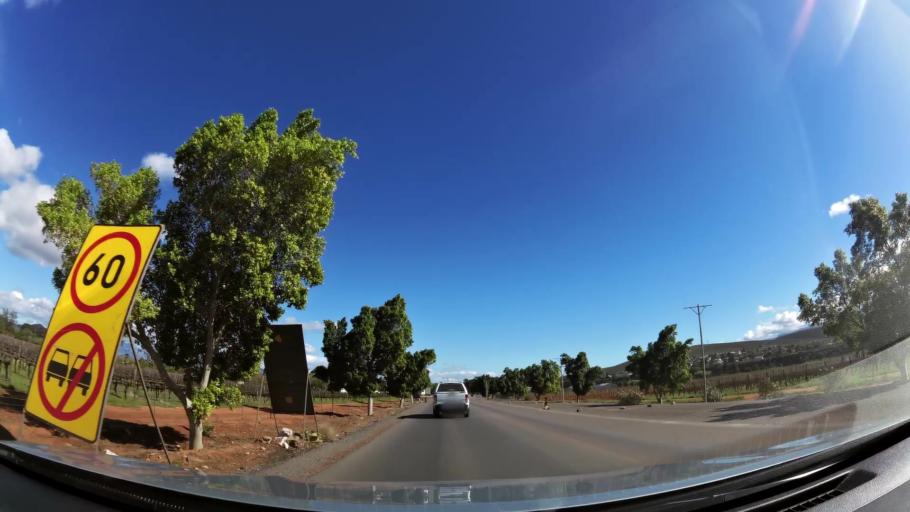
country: ZA
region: Western Cape
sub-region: Cape Winelands District Municipality
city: Ashton
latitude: -33.8319
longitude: 20.0724
